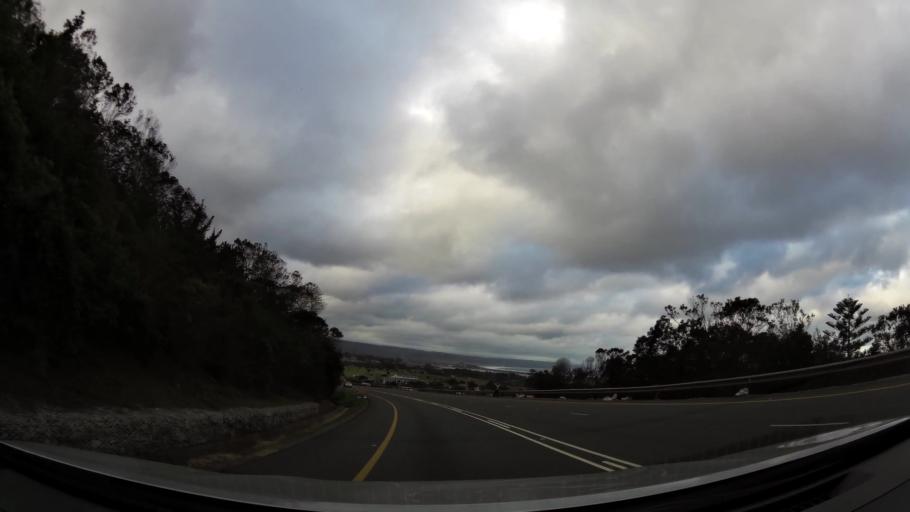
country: ZA
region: Western Cape
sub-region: Eden District Municipality
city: Plettenberg Bay
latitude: -34.0435
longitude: 23.3672
